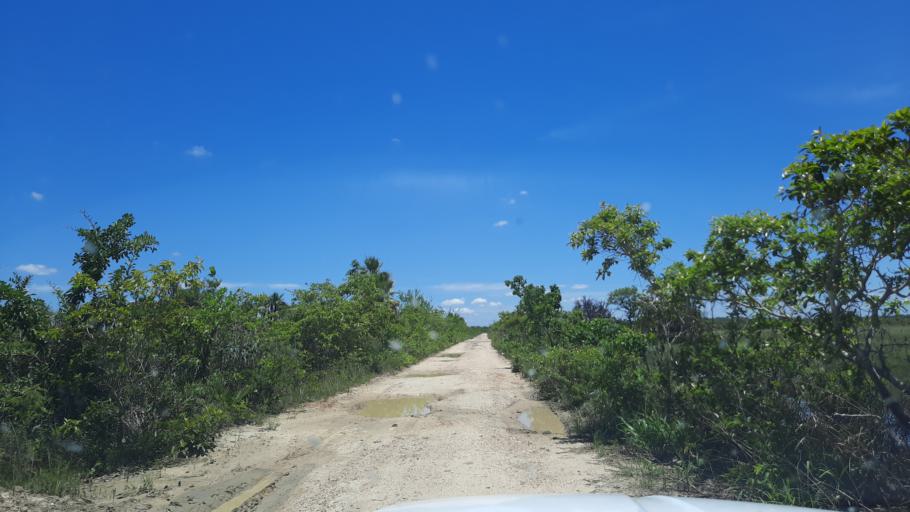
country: BZ
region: Cayo
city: Belmopan
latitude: 17.3804
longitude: -88.4912
